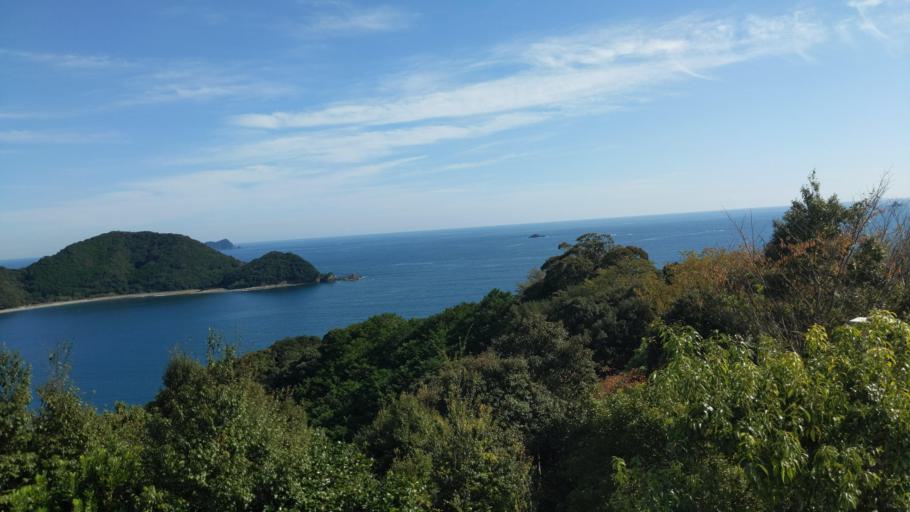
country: JP
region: Mie
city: Owase
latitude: 34.1603
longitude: 136.2876
